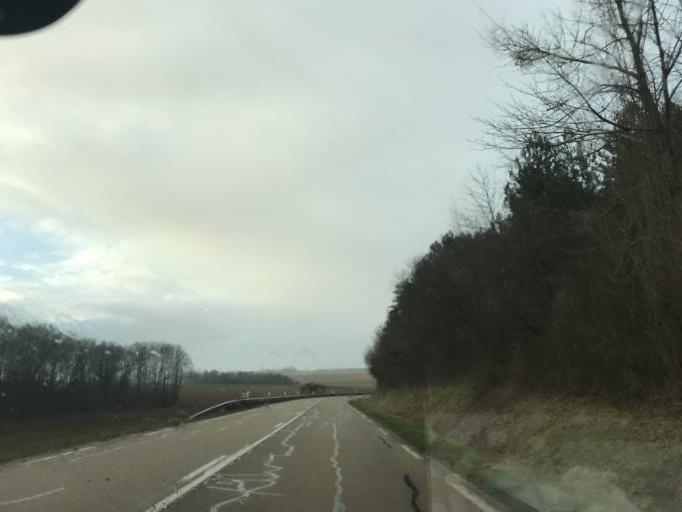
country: FR
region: Bourgogne
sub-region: Departement de l'Yonne
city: Fontenailles
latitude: 47.6309
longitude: 3.4915
